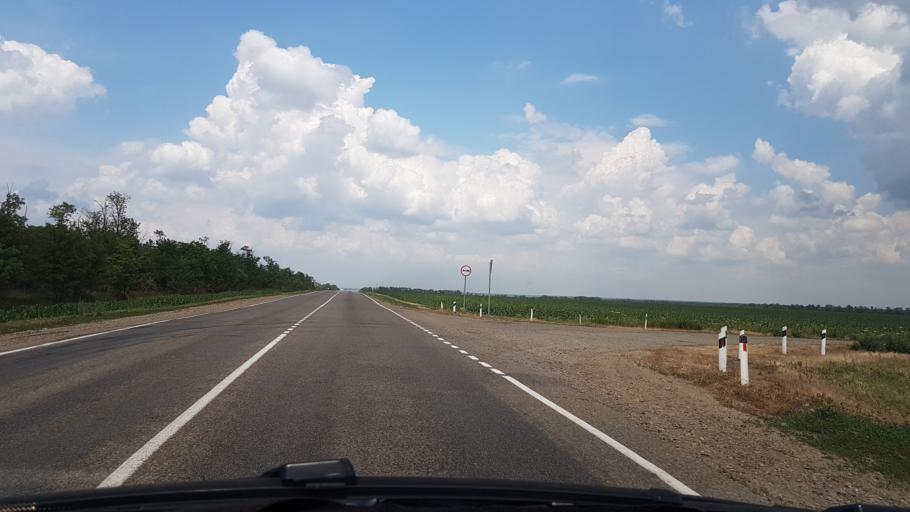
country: RU
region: Krasnodarskiy
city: Dmitriyevskaya
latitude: 45.6797
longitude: 40.7440
